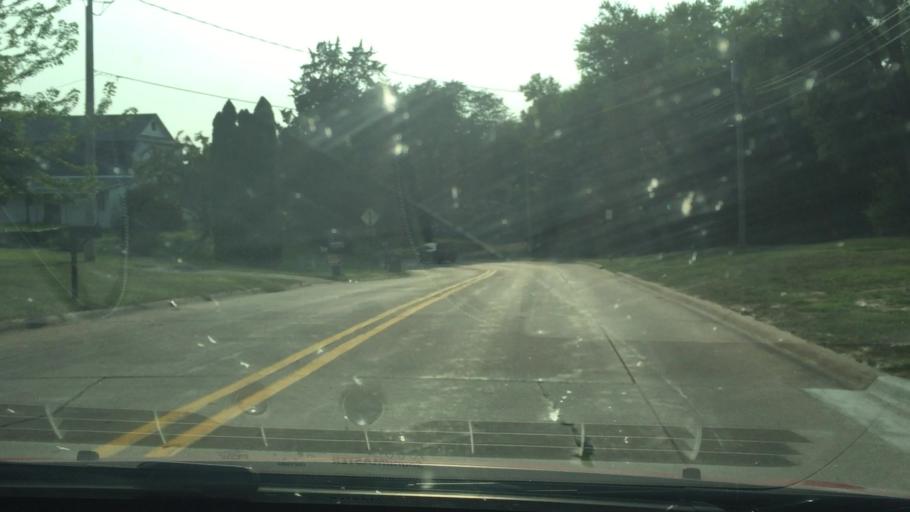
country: US
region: Iowa
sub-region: Muscatine County
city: Muscatine
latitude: 41.4474
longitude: -91.0363
